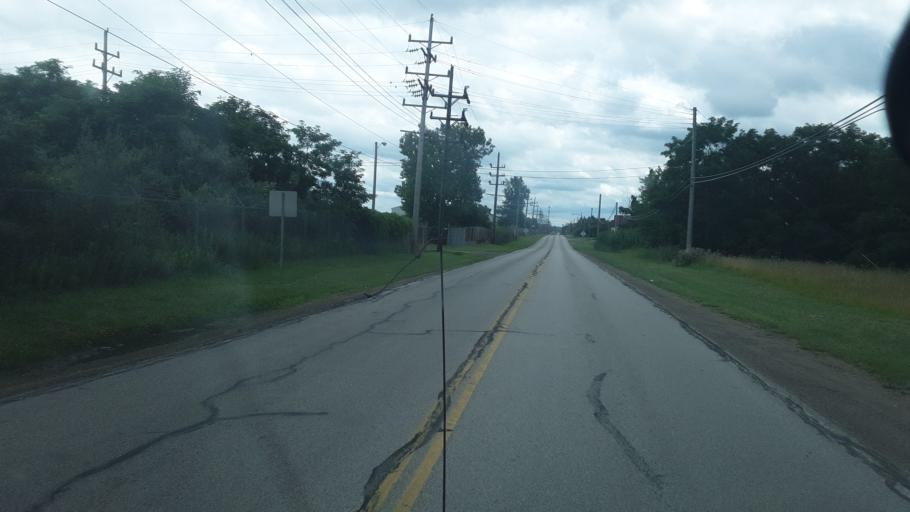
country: US
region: Ohio
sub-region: Ashtabula County
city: Edgewood
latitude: 41.9050
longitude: -80.7724
